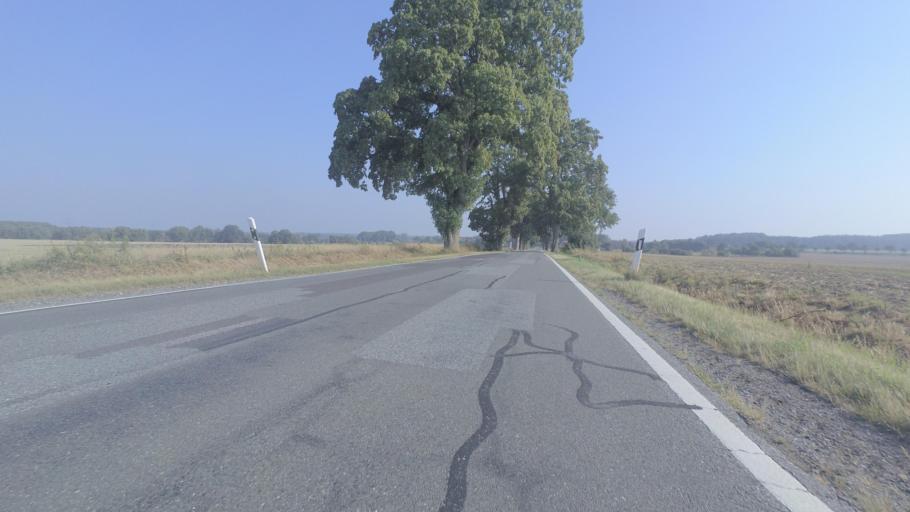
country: DE
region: Mecklenburg-Vorpommern
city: Malchow
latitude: 53.3804
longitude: 12.3901
